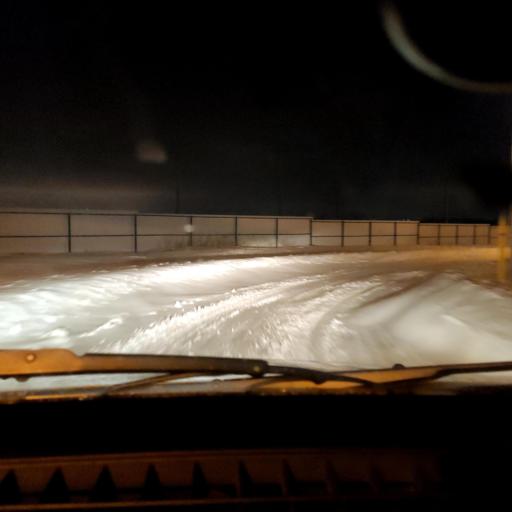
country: RU
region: Bashkortostan
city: Mikhaylovka
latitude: 54.7851
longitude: 55.8032
